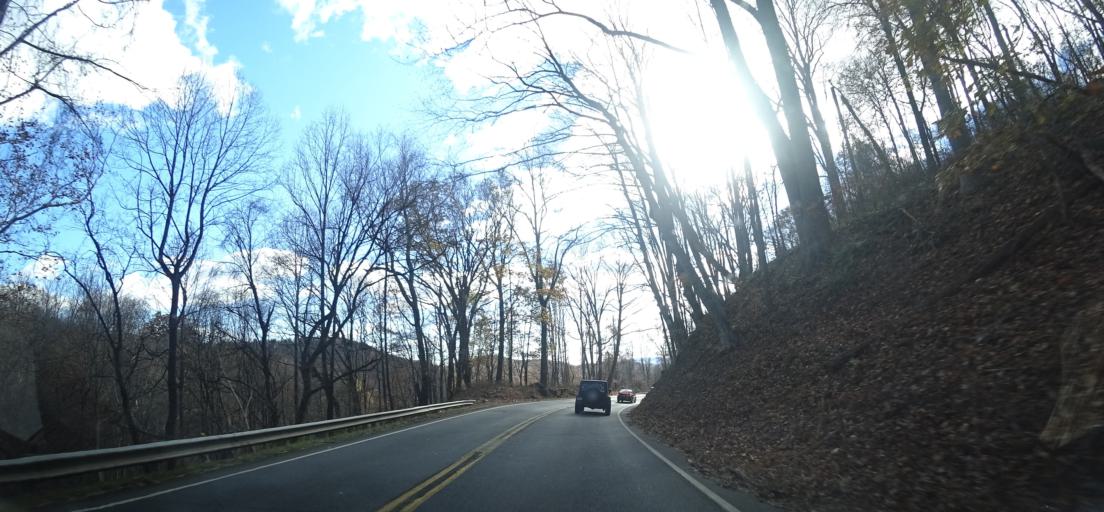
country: US
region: Virginia
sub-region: Greene County
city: Stanardsville
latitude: 38.3269
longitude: -78.4789
